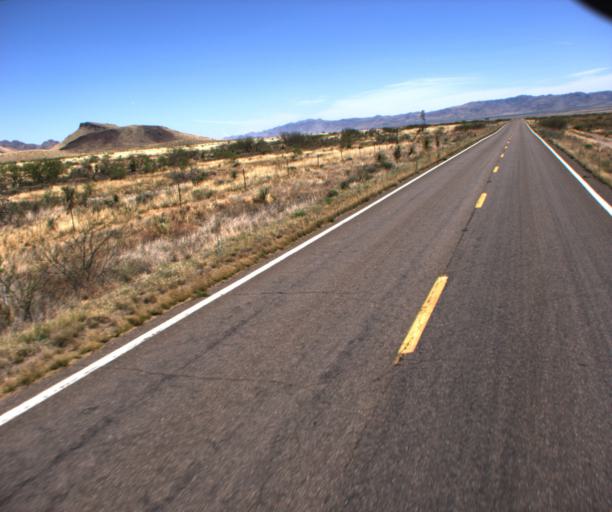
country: US
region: Arizona
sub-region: Cochise County
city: Douglas
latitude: 31.6374
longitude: -109.1844
